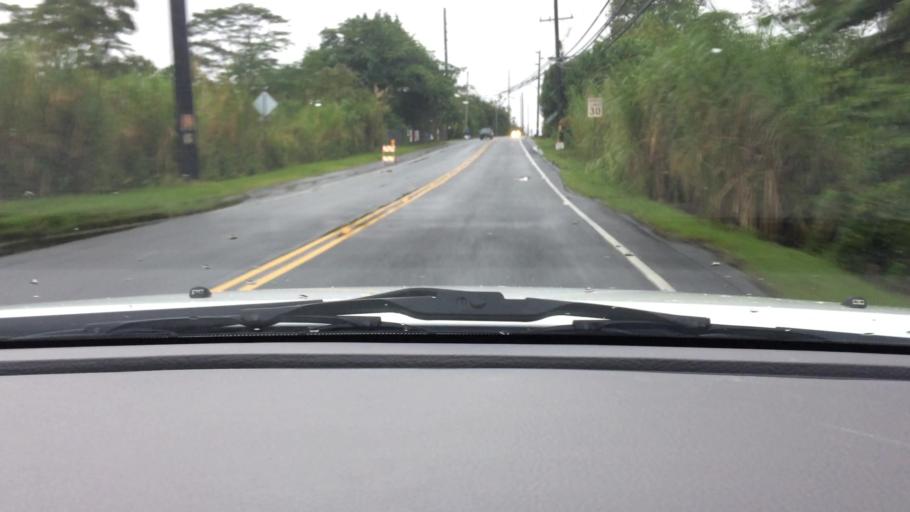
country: US
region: Hawaii
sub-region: Hawaii County
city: Hawaiian Paradise Park
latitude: 19.4994
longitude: -154.9538
